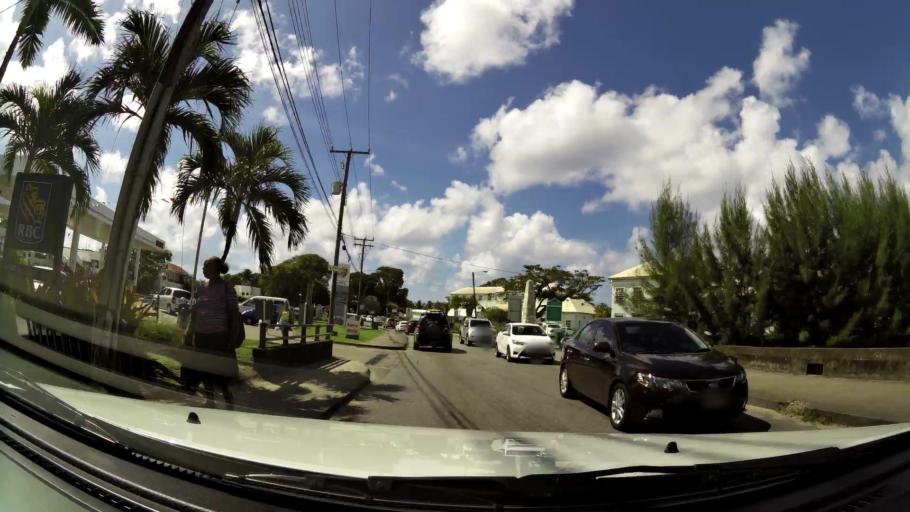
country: BB
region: Saint James
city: Holetown
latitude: 13.1859
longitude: -59.6371
